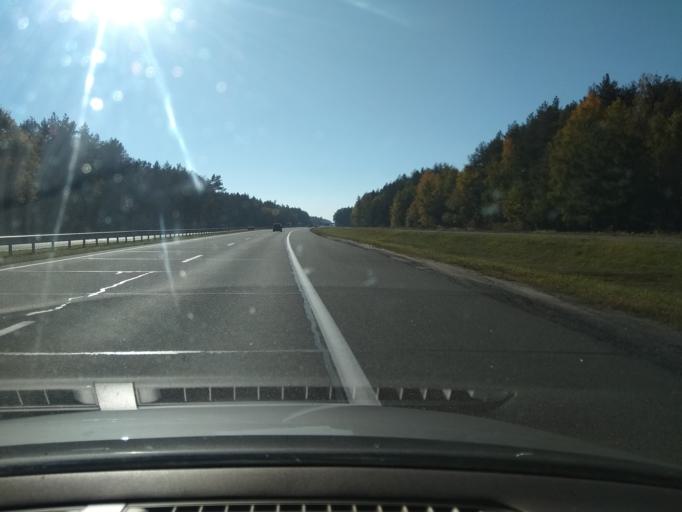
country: BY
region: Brest
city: Baranovichi
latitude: 53.0548
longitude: 25.8588
